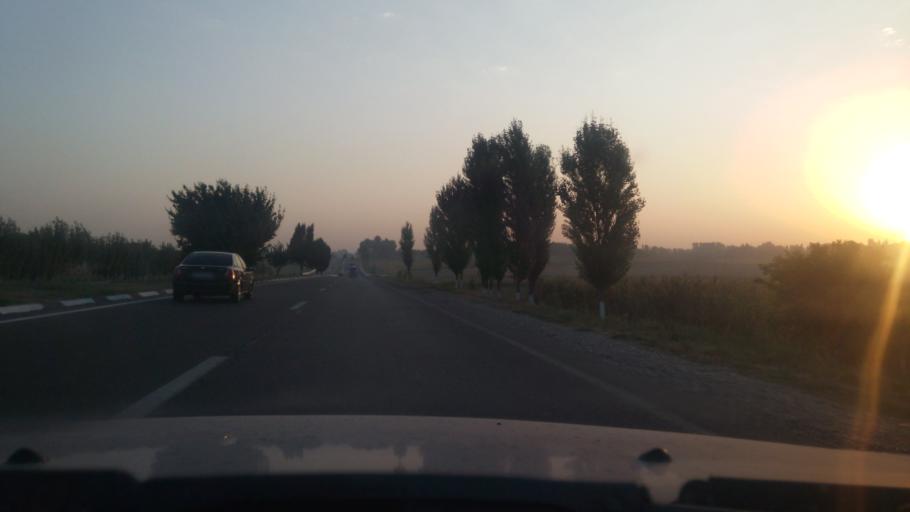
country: UZ
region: Toshkent
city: Amir Timur
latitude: 41.0939
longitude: 68.9574
